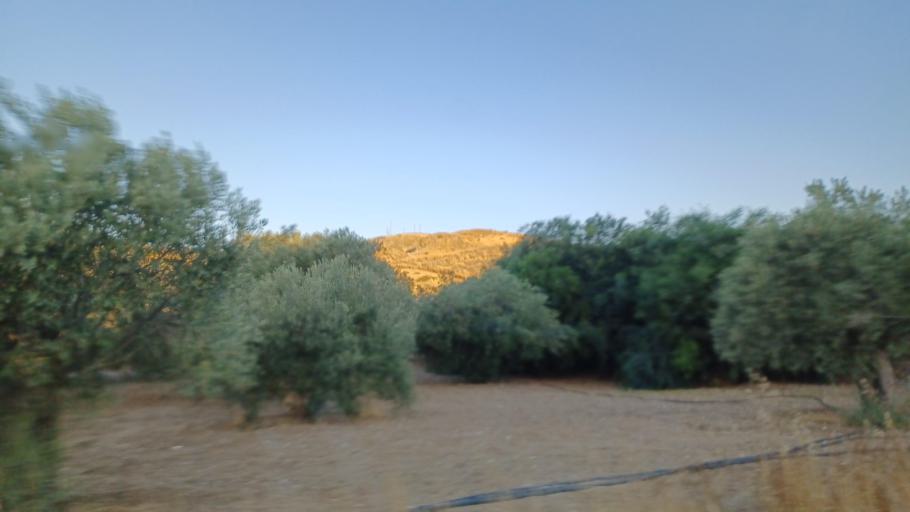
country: CY
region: Larnaka
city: Troulloi
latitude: 35.0284
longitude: 33.6290
